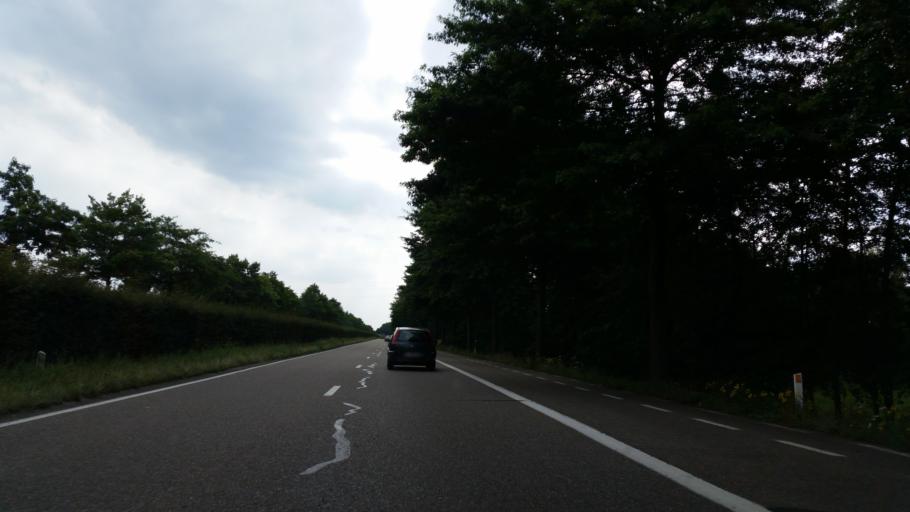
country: BE
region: Flanders
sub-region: Provincie Antwerpen
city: Geel
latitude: 51.1778
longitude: 4.9703
